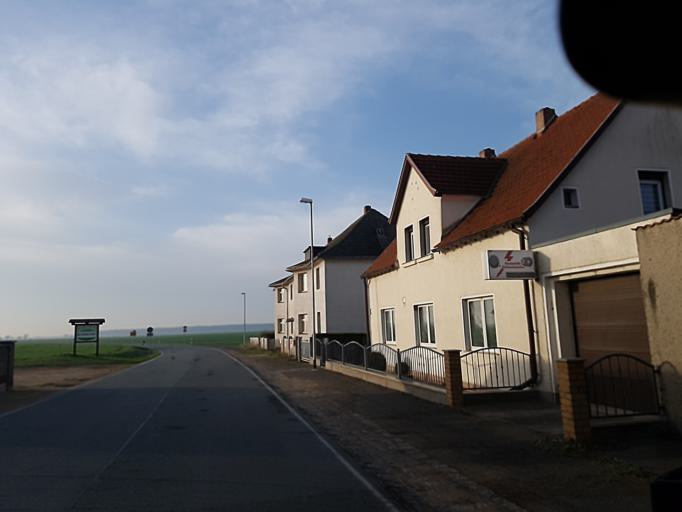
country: DE
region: Brandenburg
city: Muhlberg
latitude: 51.4027
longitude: 13.2592
